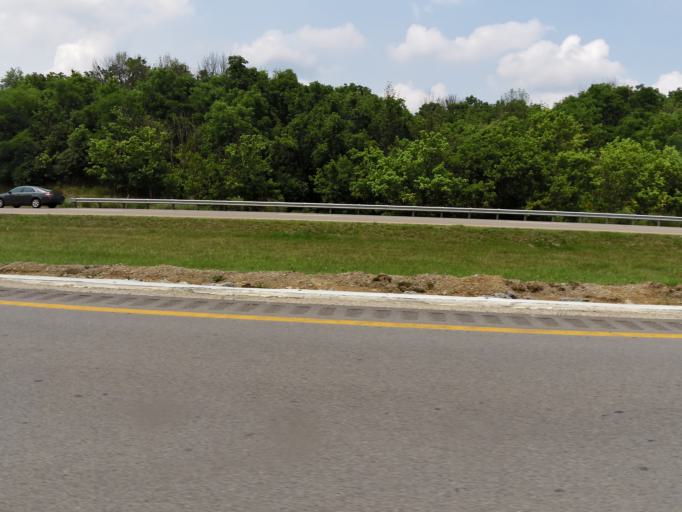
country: US
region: Kentucky
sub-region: Carroll County
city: Carrollton
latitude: 38.6532
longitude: -85.1013
